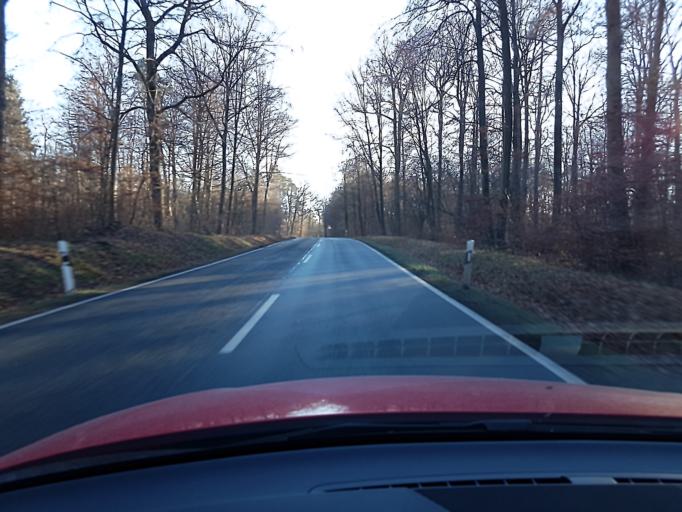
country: DE
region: Baden-Wuerttemberg
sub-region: Regierungsbezirk Stuttgart
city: Freudental
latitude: 49.0165
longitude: 9.0665
